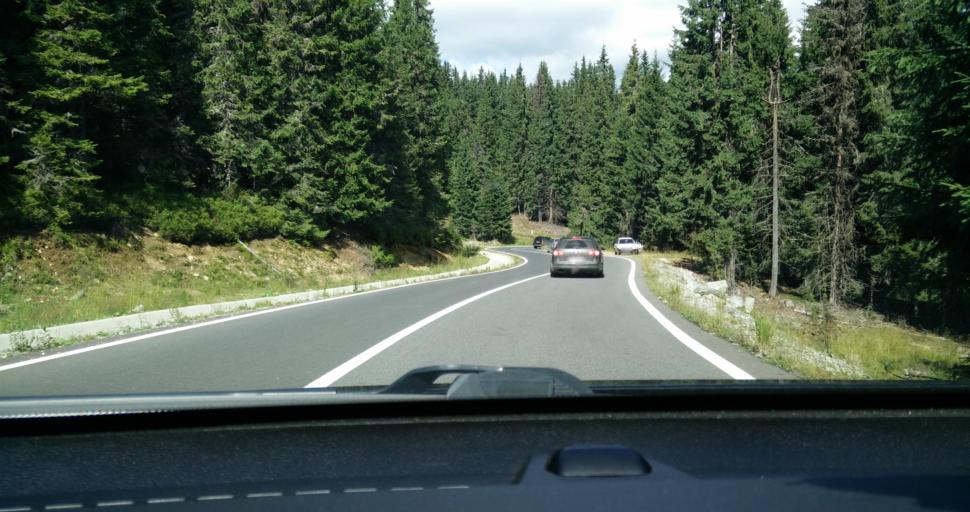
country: RO
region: Hunedoara
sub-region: Oras Petrila
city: Petrila
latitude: 45.4796
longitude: 23.6350
